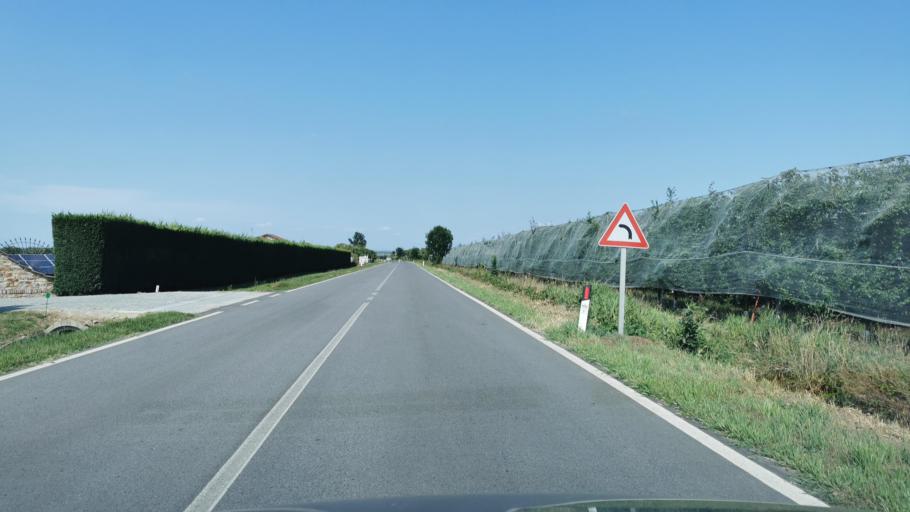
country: IT
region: Piedmont
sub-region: Provincia di Cuneo
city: Revello
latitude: 44.6715
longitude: 7.4011
